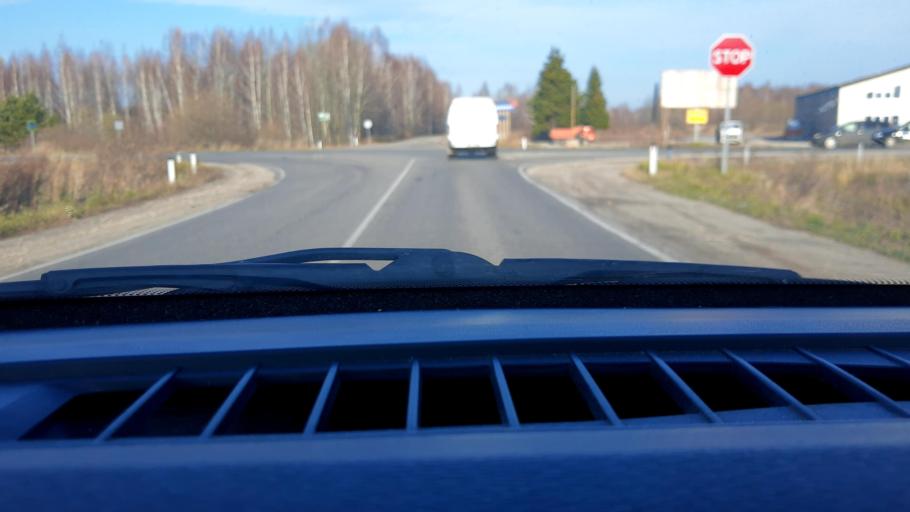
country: RU
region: Nizjnij Novgorod
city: Neklyudovo
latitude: 56.5278
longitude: 43.8319
